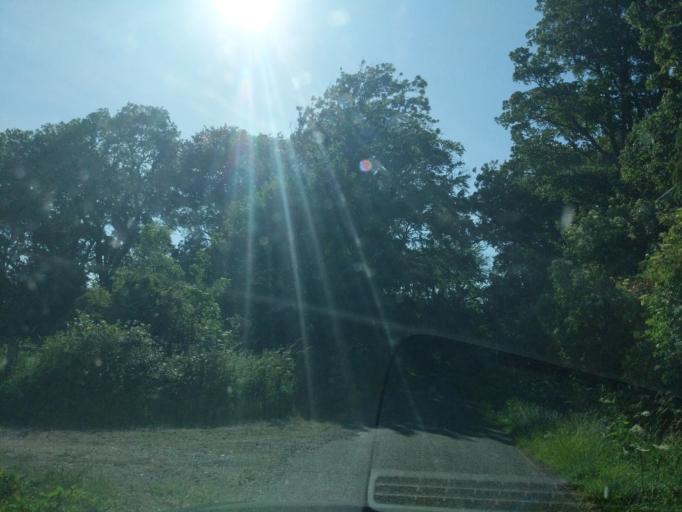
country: GB
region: Scotland
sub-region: East Lothian
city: Ormiston
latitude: 55.8784
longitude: -2.9406
